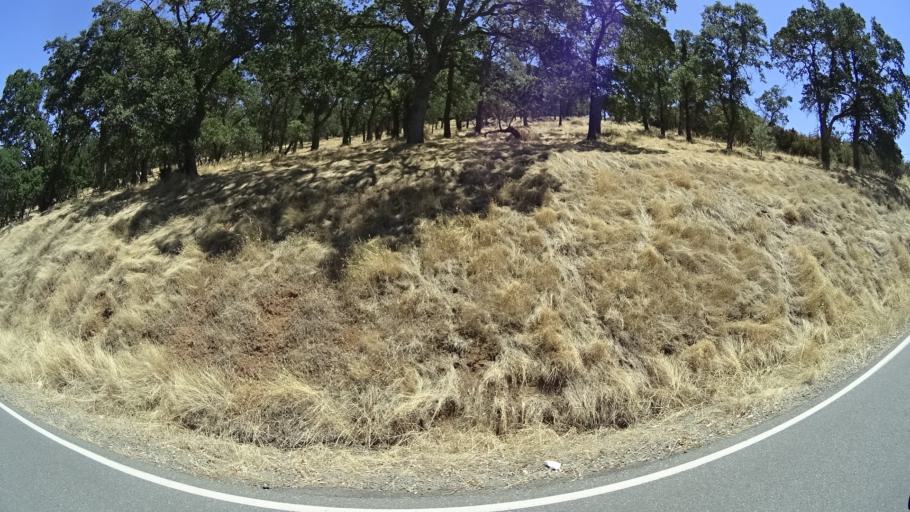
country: US
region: California
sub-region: Calaveras County
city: Rancho Calaveras
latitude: 38.1261
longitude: -120.8454
